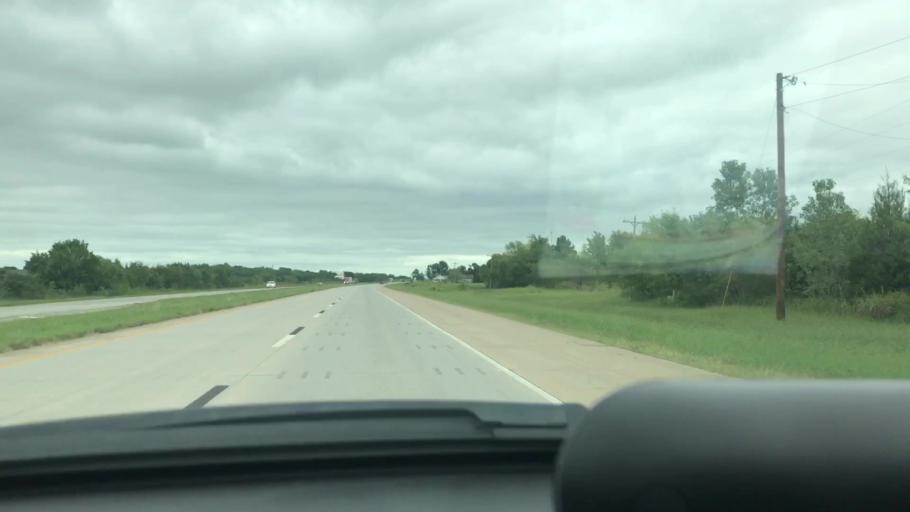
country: US
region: Oklahoma
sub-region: Mayes County
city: Chouteau
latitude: 36.0937
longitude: -95.3633
